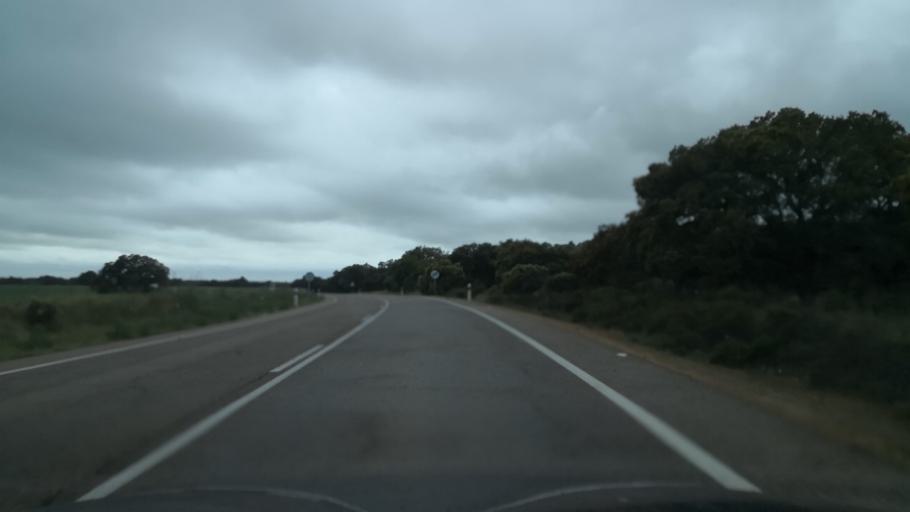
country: ES
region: Extremadura
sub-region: Provincia de Badajoz
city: Villar del Rey
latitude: 39.0468
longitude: -6.8051
